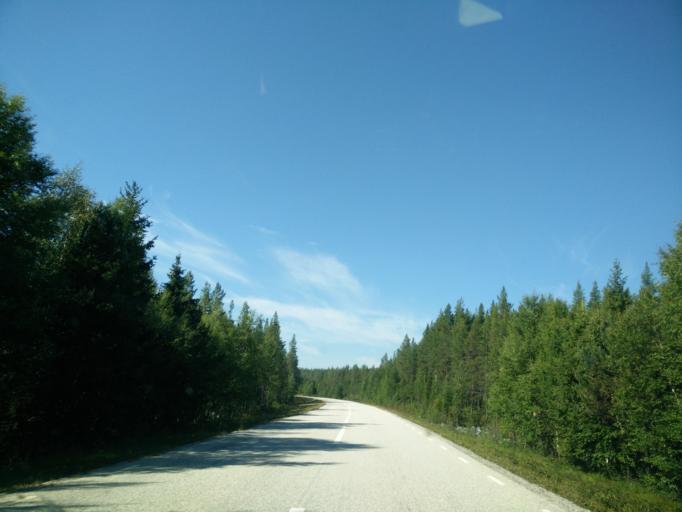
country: SE
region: Jaemtland
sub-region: Are Kommun
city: Jarpen
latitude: 62.8210
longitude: 13.5046
